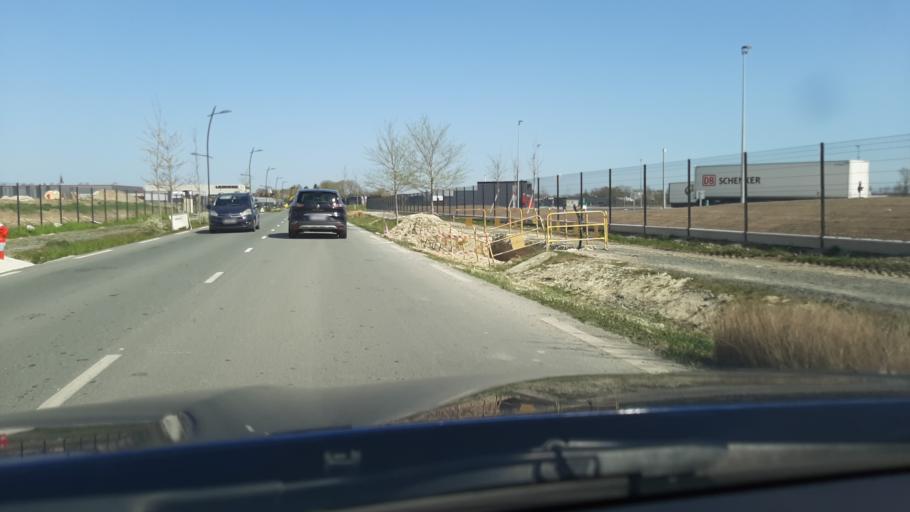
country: FR
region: Pays de la Loire
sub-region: Departement de Maine-et-Loire
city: Pellouailles-les-Vignes
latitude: 47.5167
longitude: -0.4432
